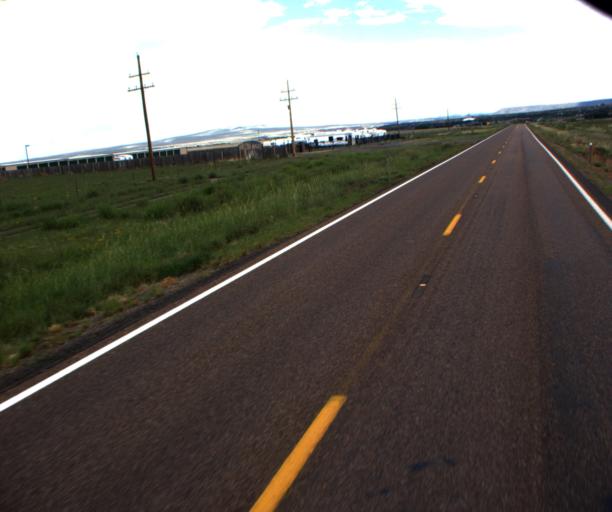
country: US
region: Arizona
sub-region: Apache County
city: Eagar
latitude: 34.1088
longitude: -109.3315
